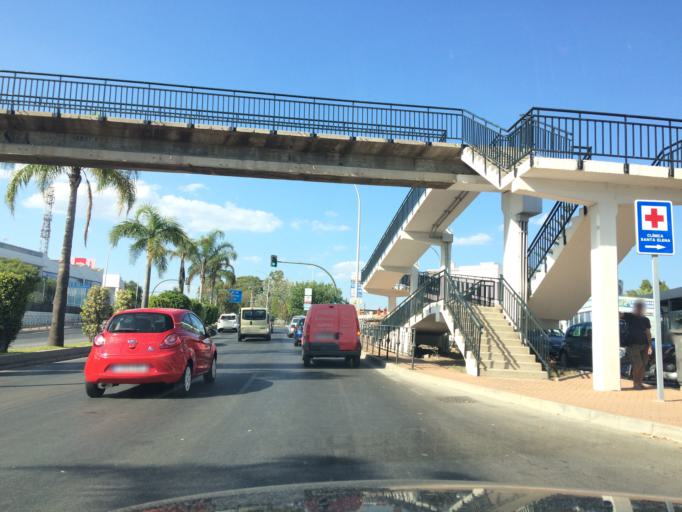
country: ES
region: Andalusia
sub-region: Provincia de Malaga
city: Torremolinos
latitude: 36.6447
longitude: -4.4902
